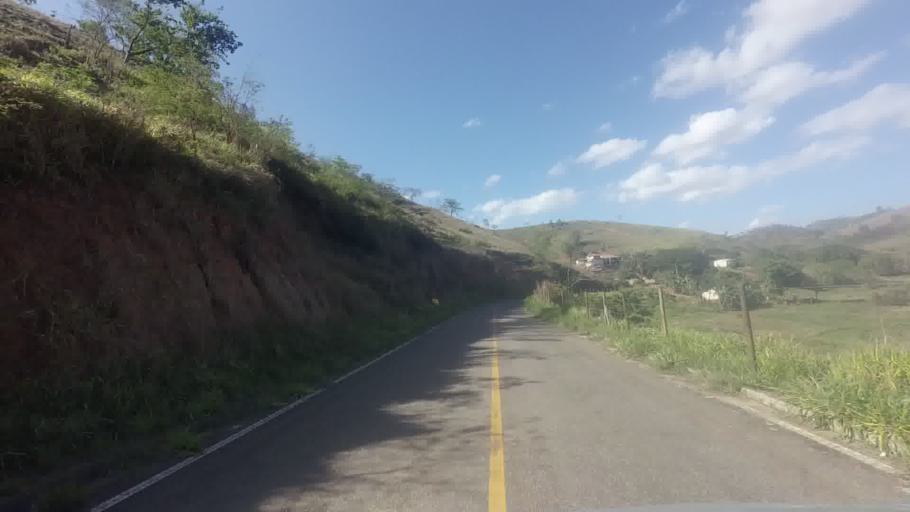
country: BR
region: Rio de Janeiro
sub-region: Bom Jesus Do Itabapoana
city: Bom Jesus do Itabapoana
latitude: -21.0994
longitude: -41.6394
